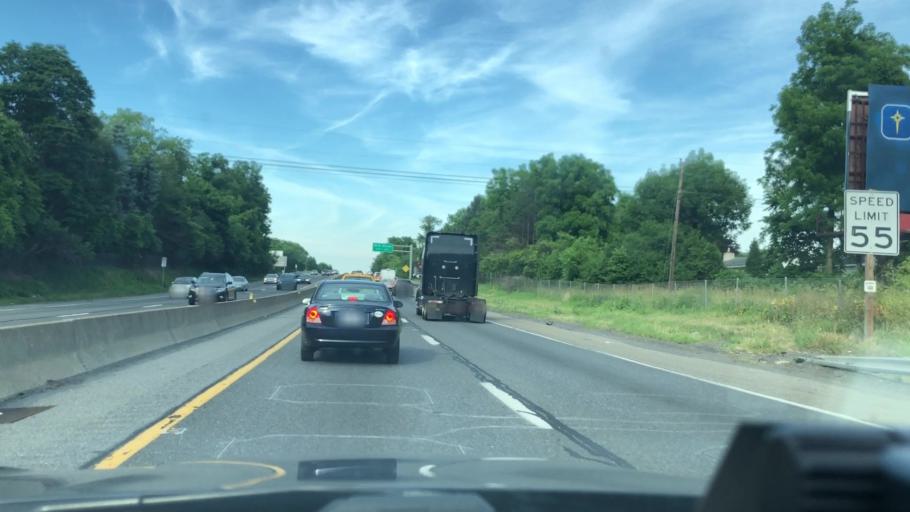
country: US
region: Pennsylvania
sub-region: Lehigh County
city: Allentown
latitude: 40.6107
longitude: -75.5221
